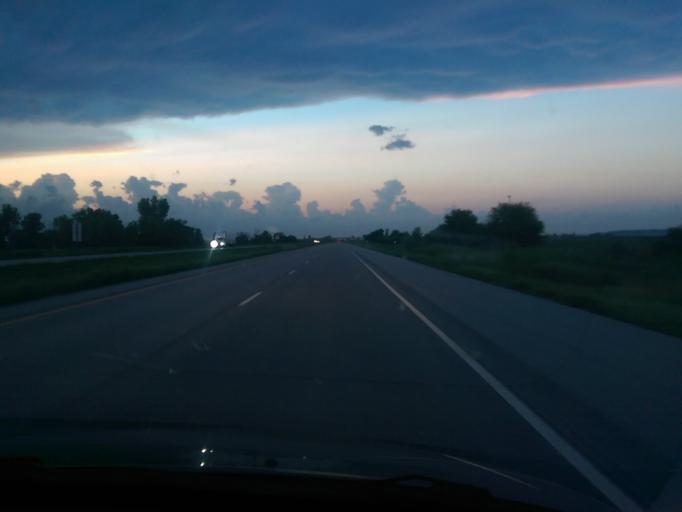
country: US
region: Nebraska
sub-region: Otoe County
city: Nebraska City
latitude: 40.7472
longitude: -95.8174
